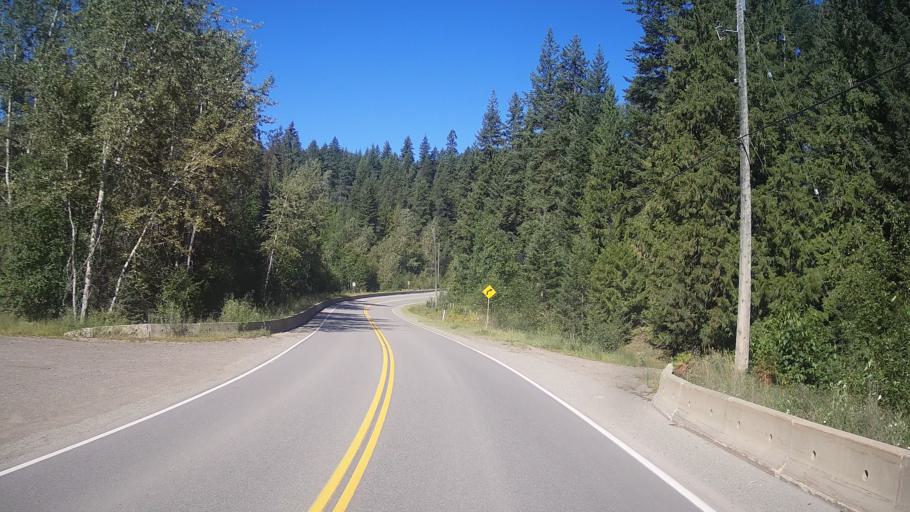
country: CA
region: British Columbia
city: Kamloops
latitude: 51.4538
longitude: -120.2191
